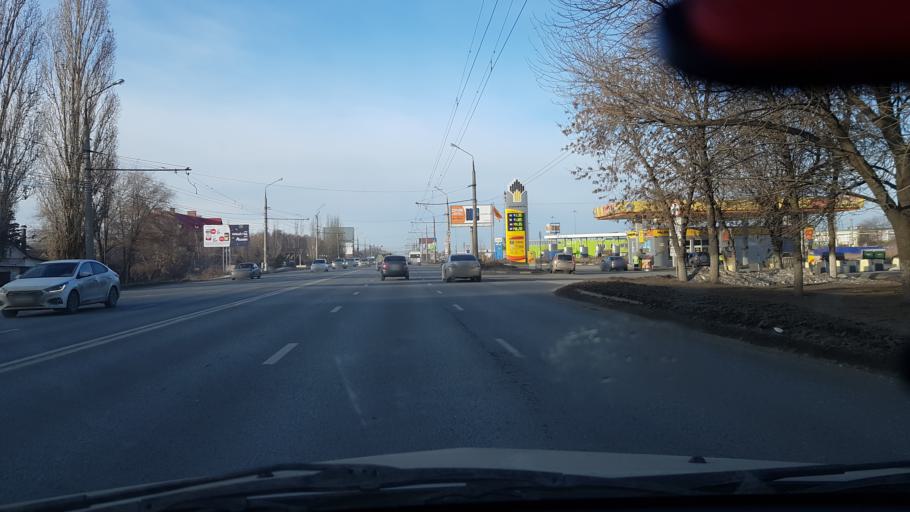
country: RU
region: Samara
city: Tol'yatti
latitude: 53.5369
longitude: 49.3928
